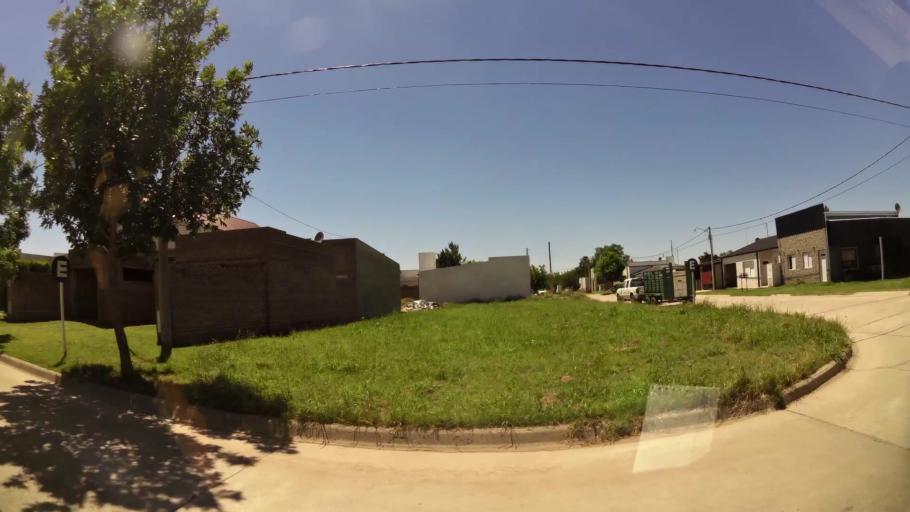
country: AR
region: Santa Fe
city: Esperanza
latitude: -31.3955
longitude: -61.0864
